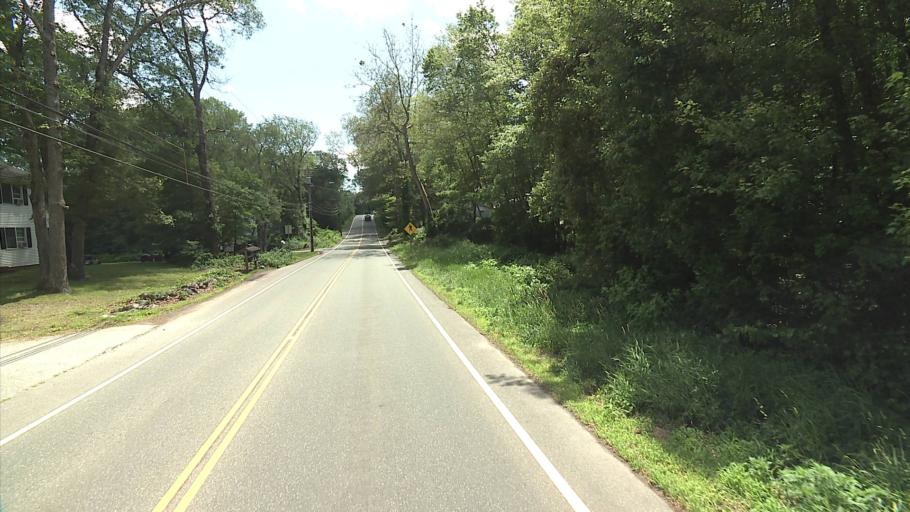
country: US
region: Connecticut
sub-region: New London County
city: Old Mystic
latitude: 41.3818
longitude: -71.9781
